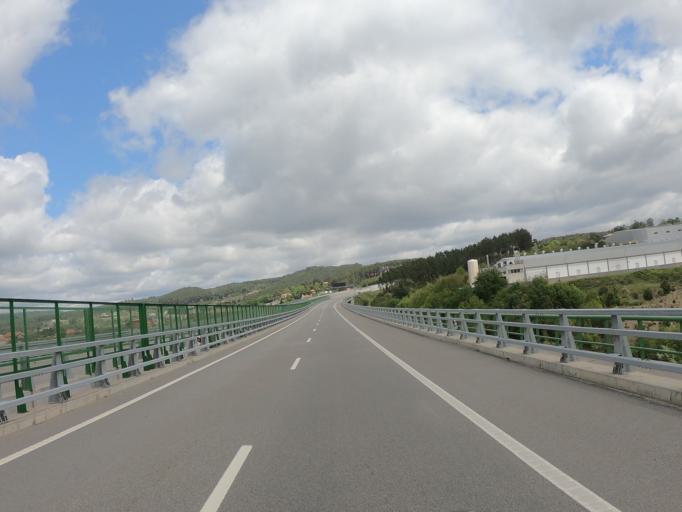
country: PT
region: Vila Real
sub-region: Vila Real
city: Vila Real
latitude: 41.2825
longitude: -7.7153
